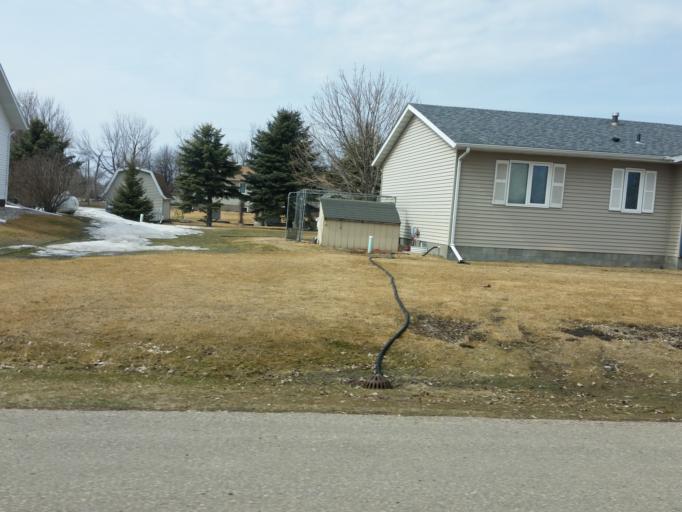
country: US
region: North Dakota
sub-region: Walsh County
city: Grafton
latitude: 48.2930
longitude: -97.3817
